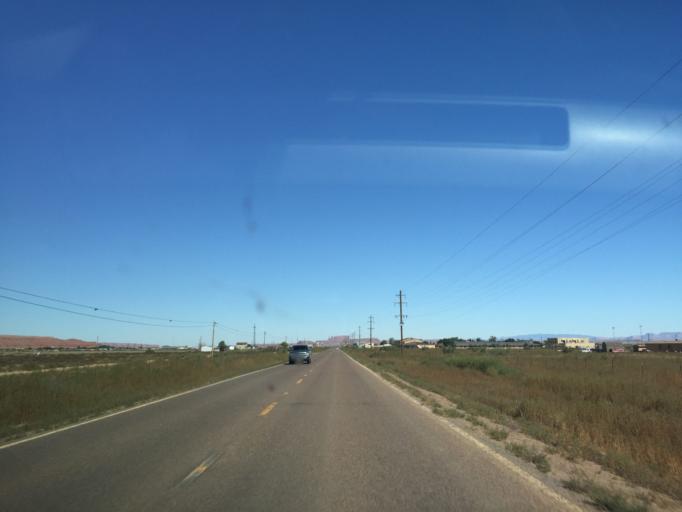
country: US
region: Arizona
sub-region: Apache County
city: Many Farms
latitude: 36.3433
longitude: -109.6220
